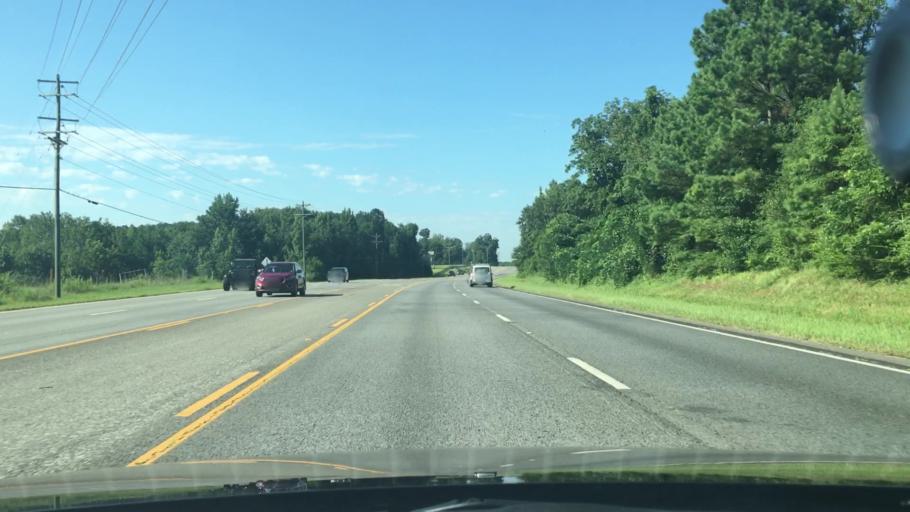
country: US
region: Georgia
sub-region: Pike County
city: Zebulon
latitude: 33.1640
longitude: -84.3070
